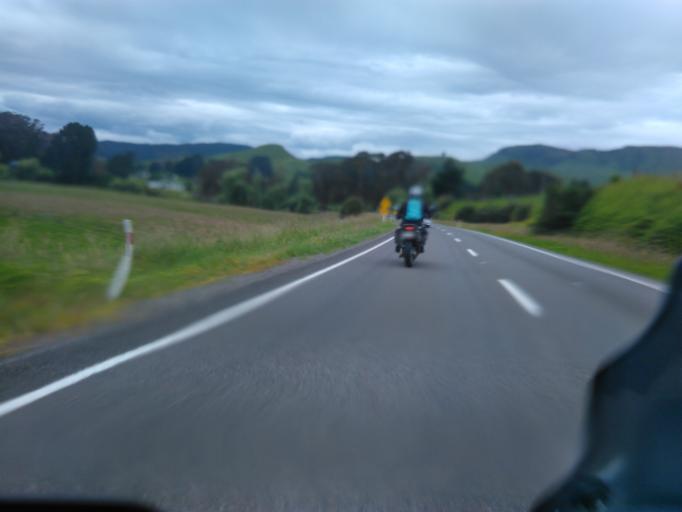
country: NZ
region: Bay of Plenty
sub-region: Opotiki District
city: Opotiki
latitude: -38.3602
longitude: 177.5261
